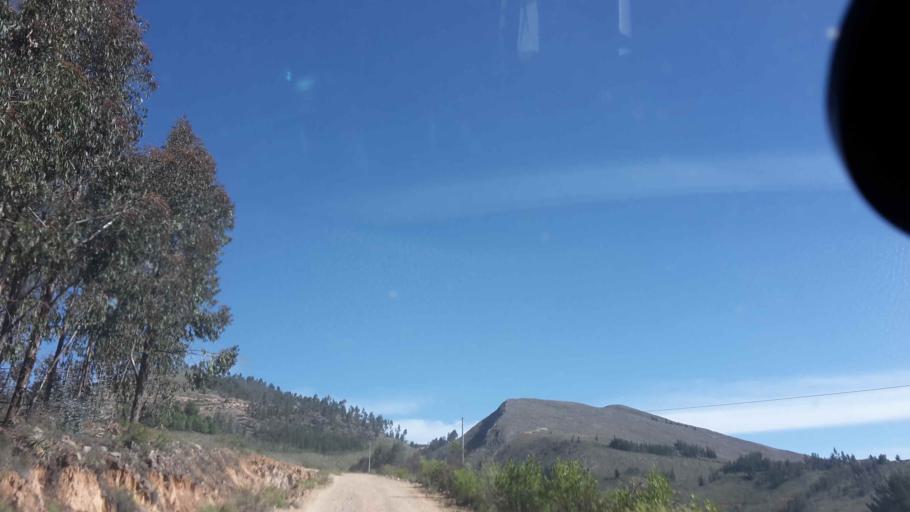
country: BO
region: Cochabamba
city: Arani
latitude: -17.6577
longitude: -65.7387
